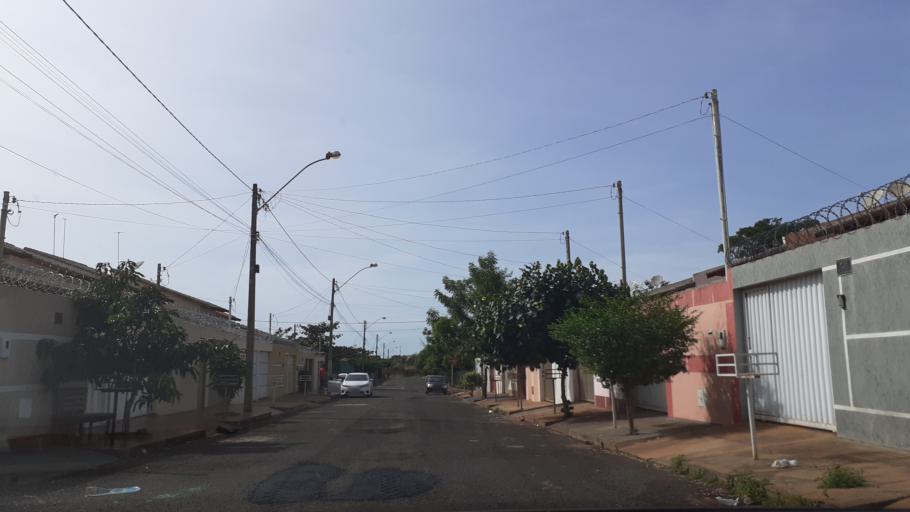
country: BR
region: Goias
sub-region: Itumbiara
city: Itumbiara
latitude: -18.4246
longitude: -49.2454
